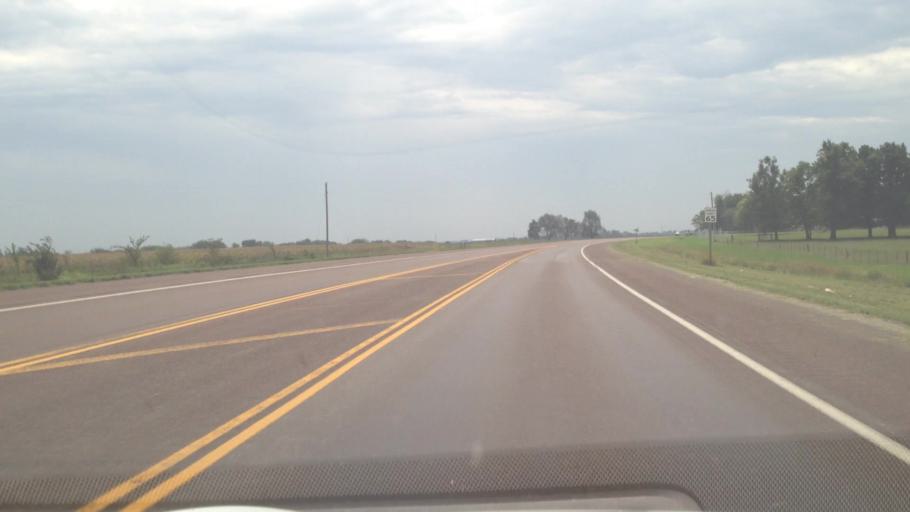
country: US
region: Kansas
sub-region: Crawford County
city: Girard
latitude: 37.4679
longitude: -94.8336
